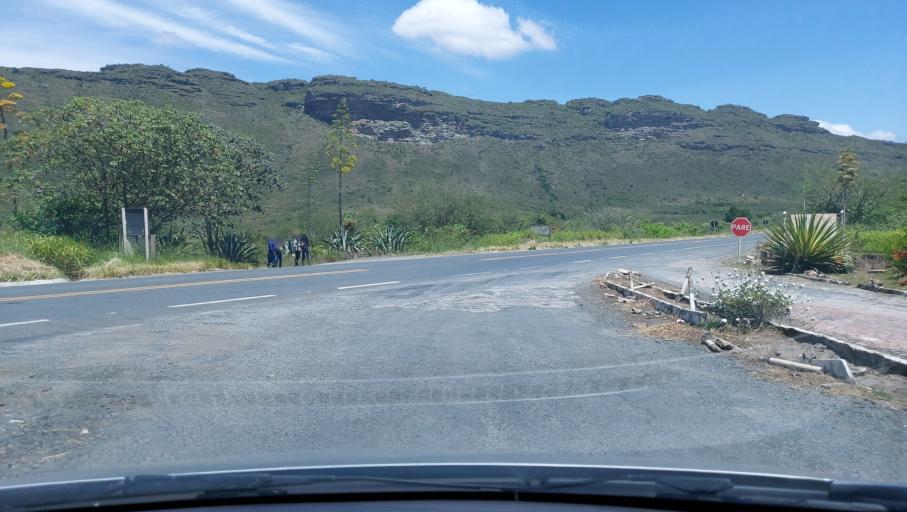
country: BR
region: Bahia
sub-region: Iraquara
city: Iraquara
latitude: -12.4616
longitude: -41.4673
